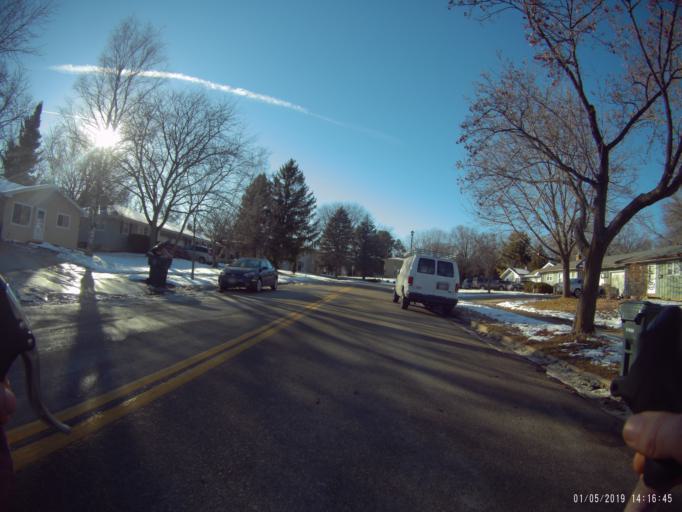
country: US
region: Wisconsin
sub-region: Dane County
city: Shorewood Hills
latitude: 43.0248
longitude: -89.4591
